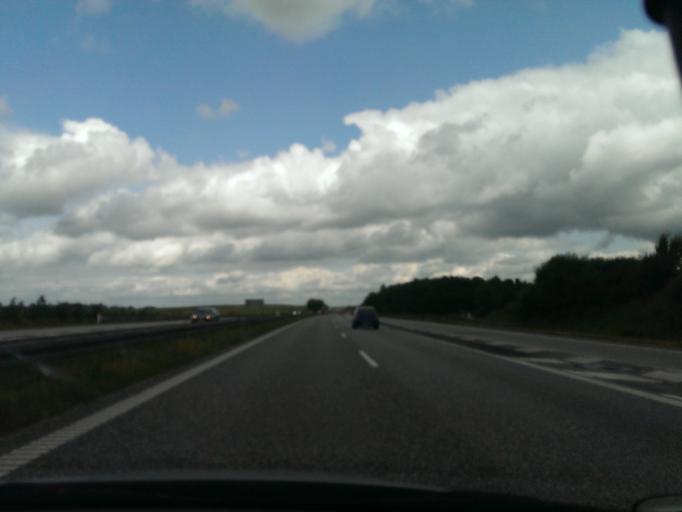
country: DK
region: North Denmark
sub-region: Mariagerfjord Kommune
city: Hobro
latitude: 56.5926
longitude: 9.7677
